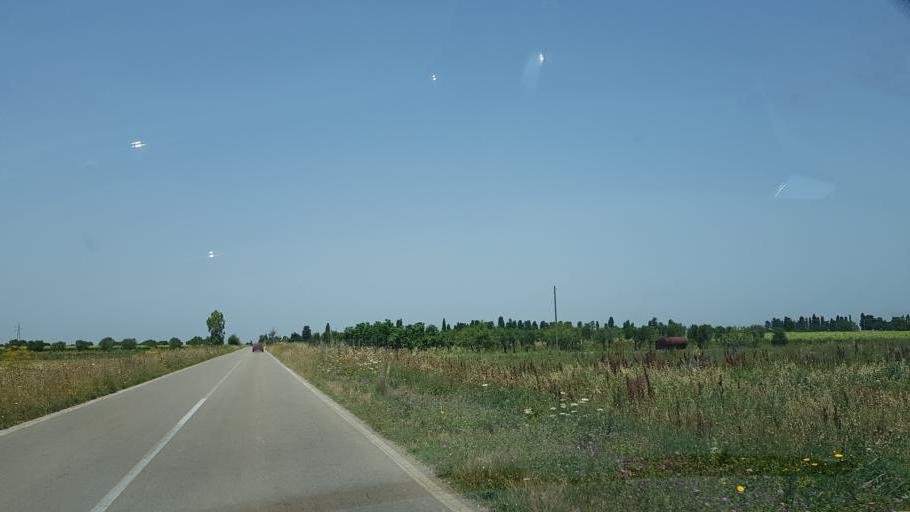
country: IT
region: Apulia
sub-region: Provincia di Brindisi
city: San Pancrazio Salentino
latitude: 40.3806
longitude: 17.8370
